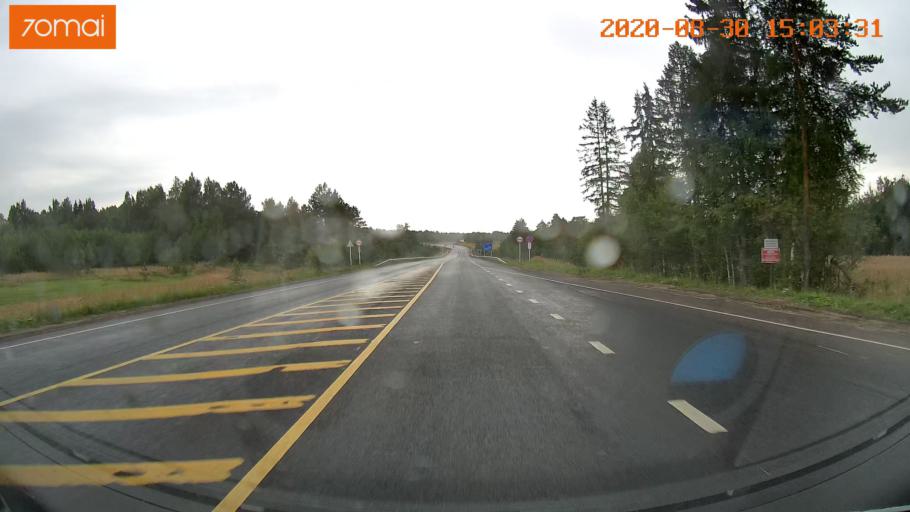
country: RU
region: Ivanovo
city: Staraya Vichuga
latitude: 57.2982
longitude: 41.9113
